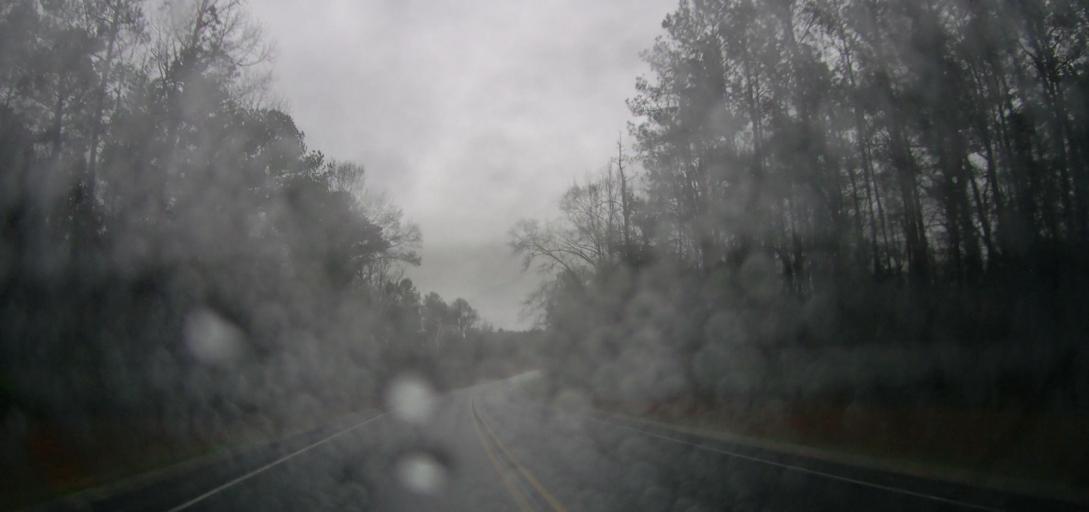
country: US
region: Alabama
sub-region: Chilton County
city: Clanton
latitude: 32.6114
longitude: -86.7193
